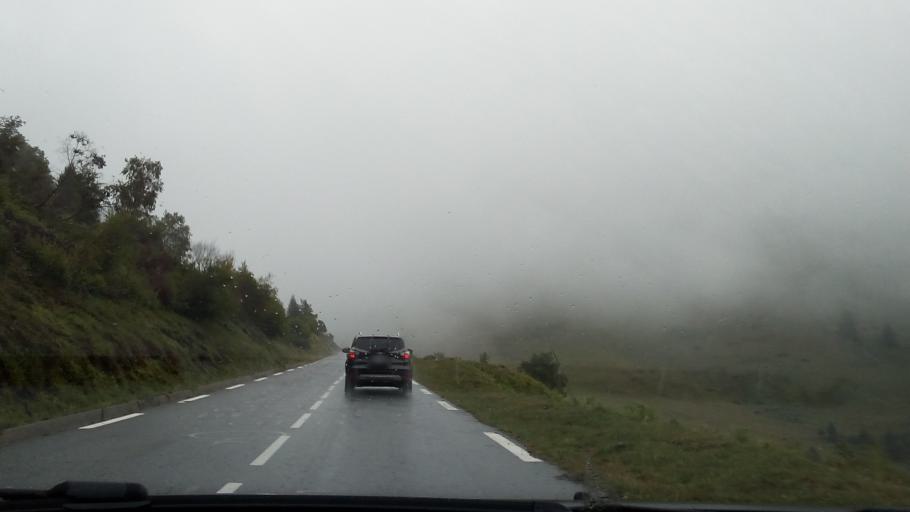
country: FR
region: Midi-Pyrenees
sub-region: Departement des Hautes-Pyrenees
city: Luz-Saint-Sauveur
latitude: 42.9066
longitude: 0.1024
